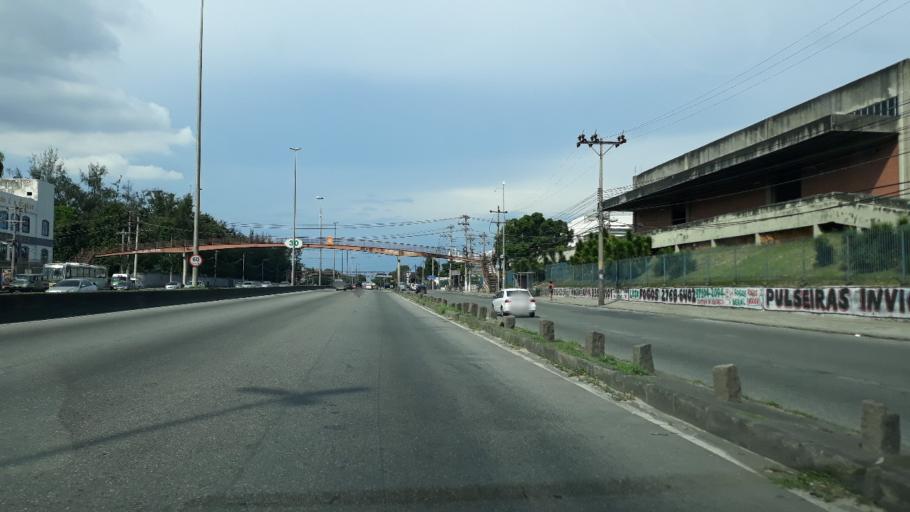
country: BR
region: Rio de Janeiro
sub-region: Sao Joao De Meriti
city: Sao Joao de Meriti
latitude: -22.8420
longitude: -43.3720
